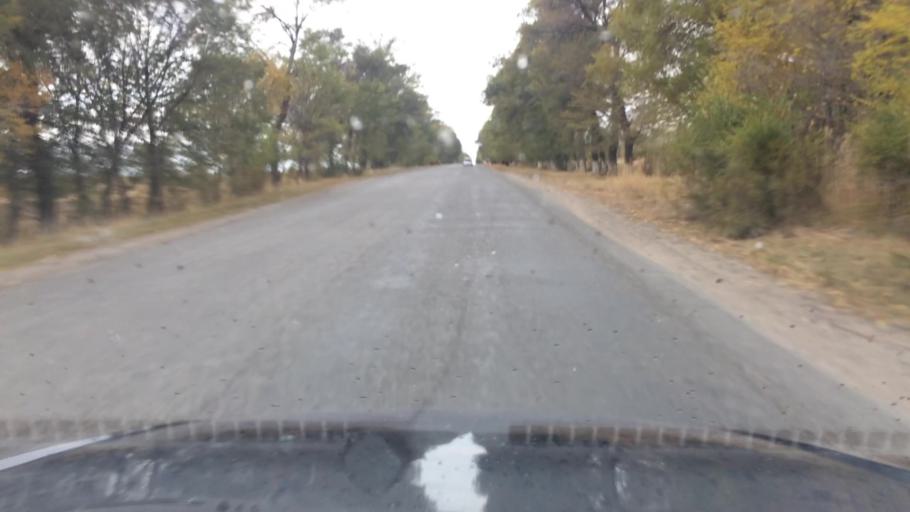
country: KG
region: Ysyk-Koel
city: Tyup
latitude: 42.7374
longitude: 77.9952
